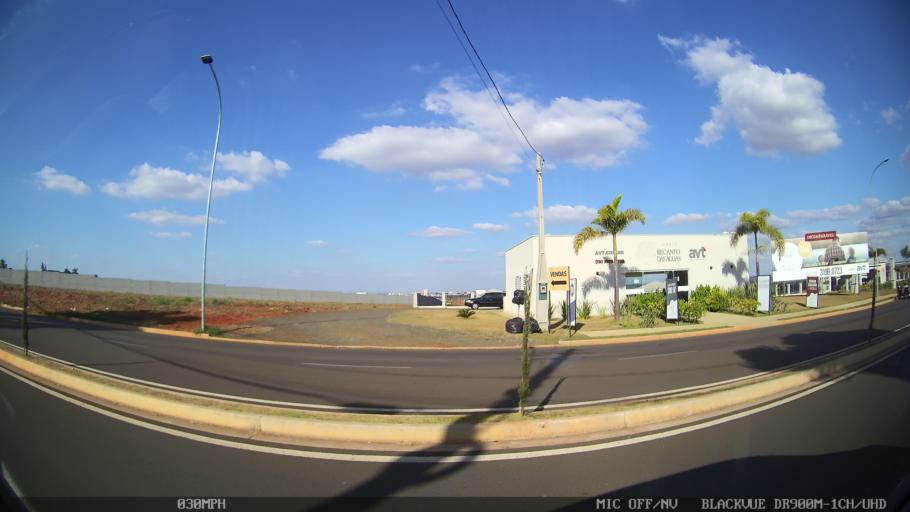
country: BR
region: Sao Paulo
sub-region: Nova Odessa
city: Nova Odessa
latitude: -22.8107
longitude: -47.3208
